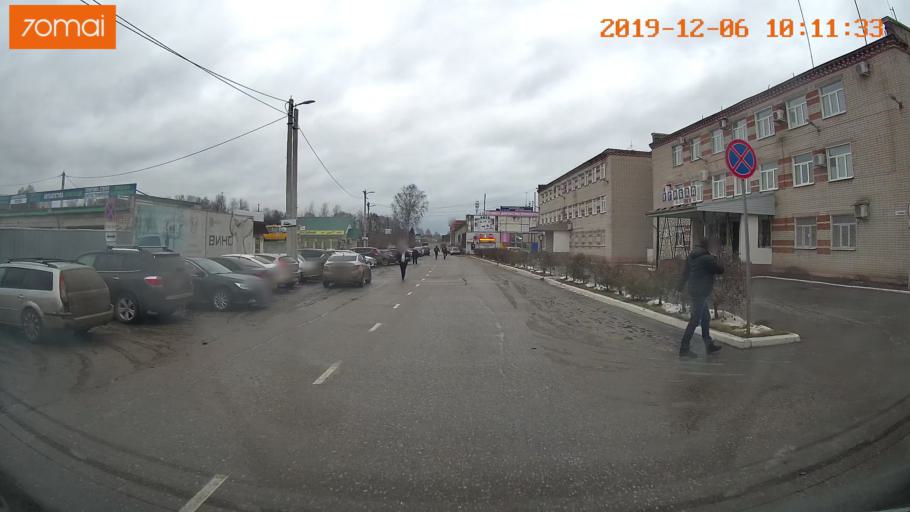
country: RU
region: Ivanovo
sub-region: Gorod Ivanovo
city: Ivanovo
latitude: 57.0311
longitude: 40.9749
